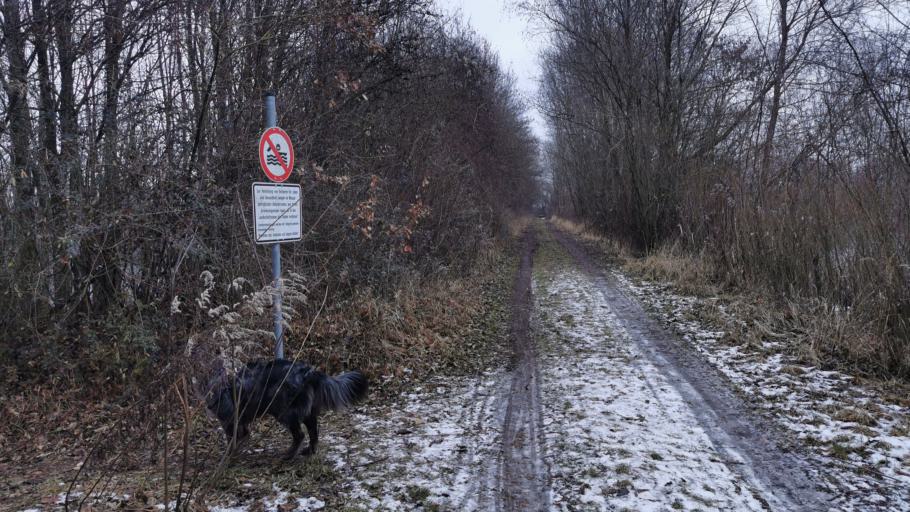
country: DE
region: Bavaria
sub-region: Upper Bavaria
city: Kirchheim bei Muenchen
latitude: 48.1929
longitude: 11.7603
